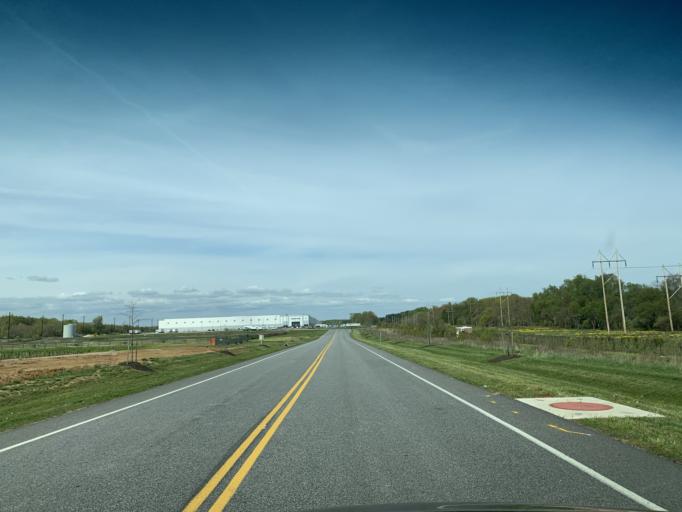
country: US
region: Maryland
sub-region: Harford County
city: Perryman
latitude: 39.4749
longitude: -76.1873
